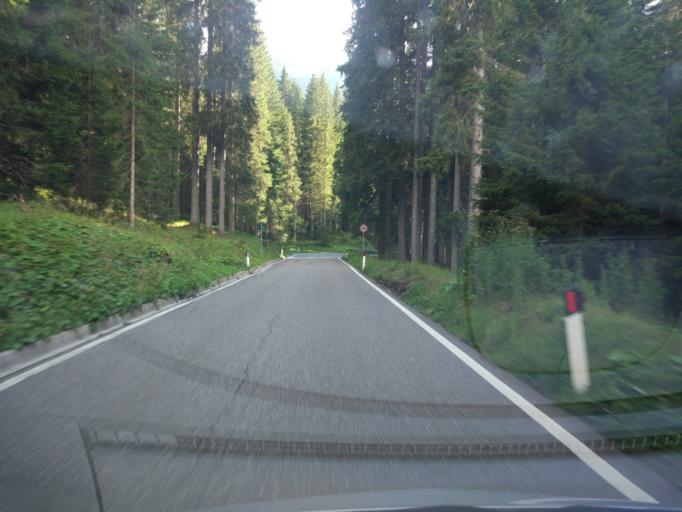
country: IT
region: Veneto
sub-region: Provincia di Belluno
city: Falcade Alto
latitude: 46.3038
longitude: 11.7593
